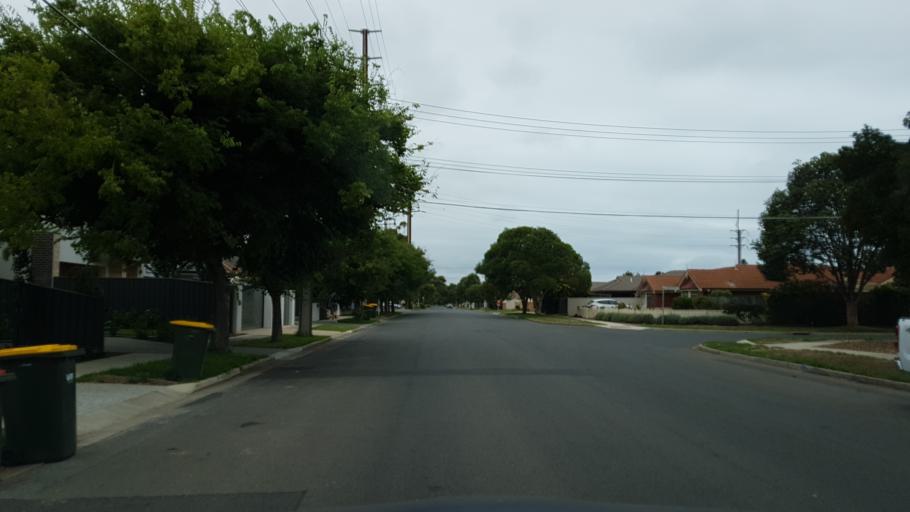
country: AU
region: South Australia
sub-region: Charles Sturt
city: Henley Beach
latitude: -34.9274
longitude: 138.5075
